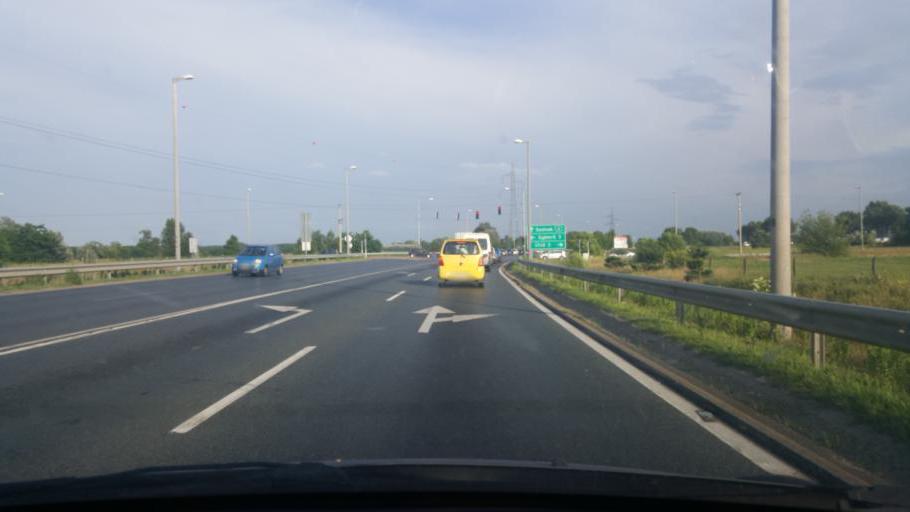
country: HU
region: Pest
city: Ullo
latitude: 47.3951
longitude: 19.3658
